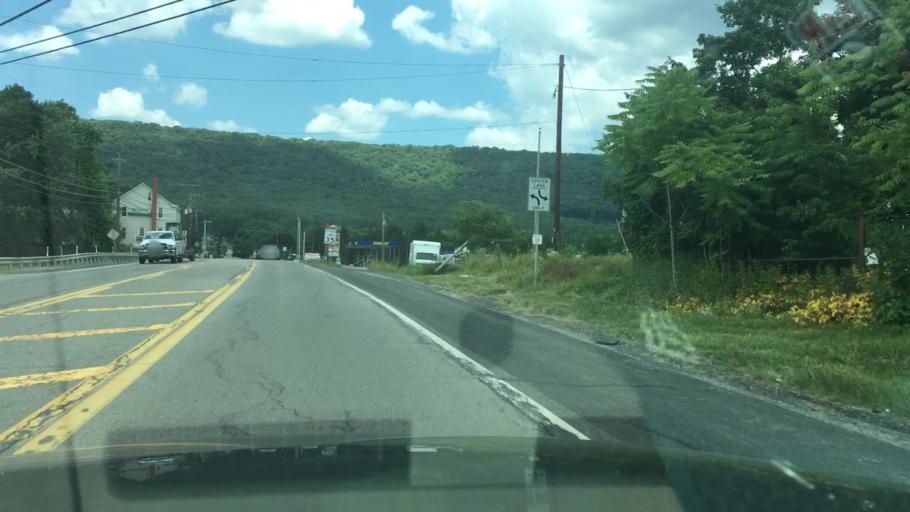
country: US
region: Pennsylvania
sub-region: Schuylkill County
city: Ashland
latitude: 40.7579
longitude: -76.3824
